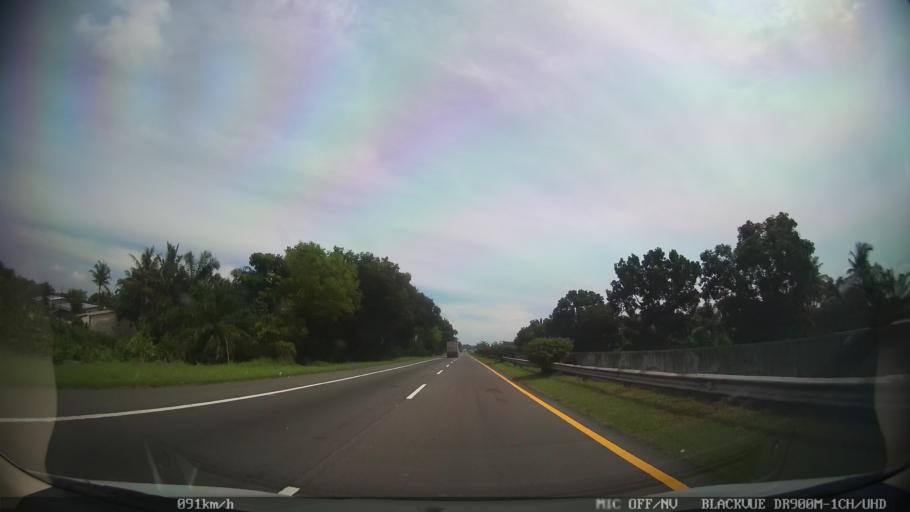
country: ID
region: North Sumatra
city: Labuhan Deli
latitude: 3.7044
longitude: 98.6815
